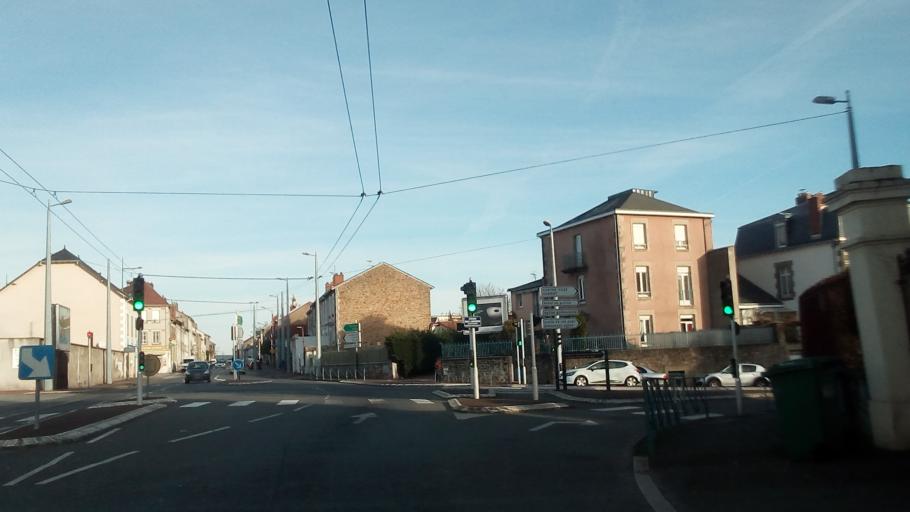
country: FR
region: Limousin
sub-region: Departement de la Haute-Vienne
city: Limoges
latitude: 45.8441
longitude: 1.2457
